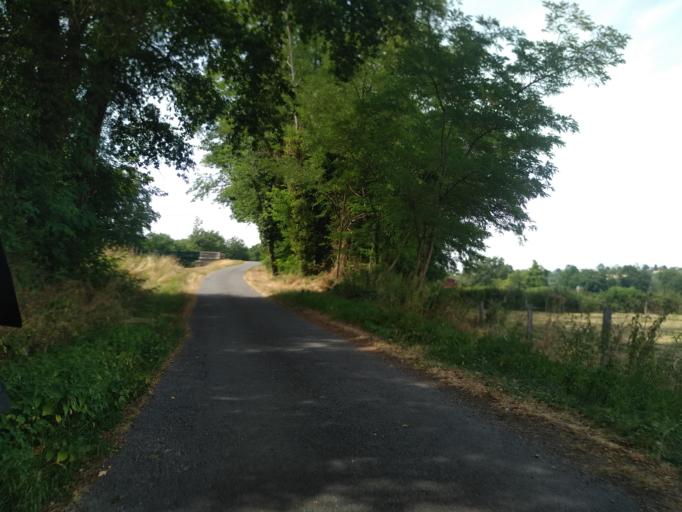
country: FR
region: Auvergne
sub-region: Departement de l'Allier
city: Diou
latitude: 46.5312
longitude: 3.7694
